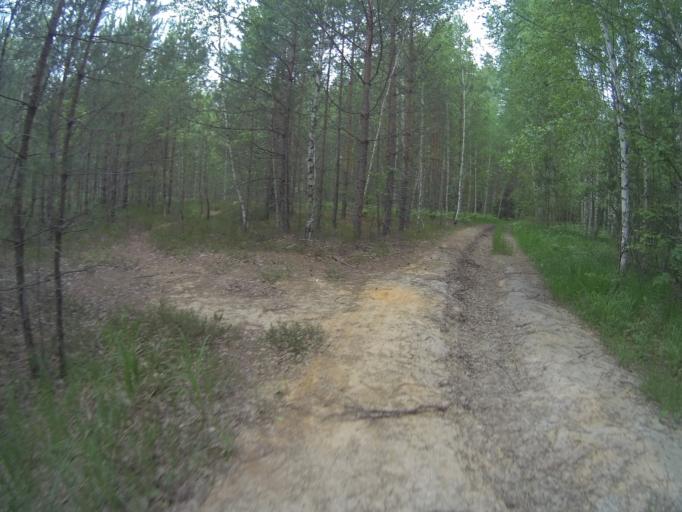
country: RU
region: Vladimir
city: Raduzhnyy
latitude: 55.9708
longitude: 40.2605
